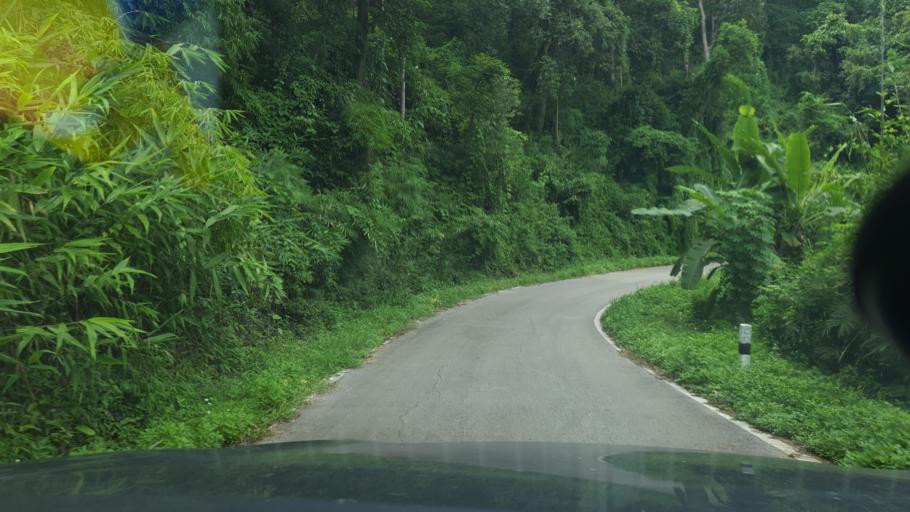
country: TH
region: Lampang
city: Hang Chat
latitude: 18.4193
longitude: 99.2633
